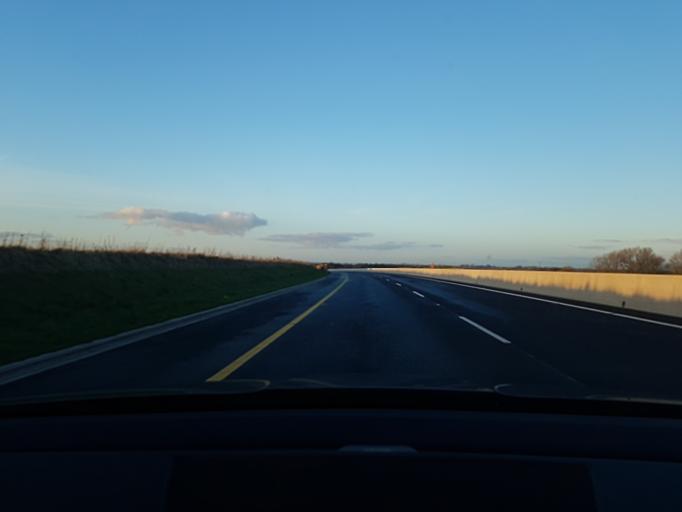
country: IE
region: Connaught
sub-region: County Galway
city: Tuam
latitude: 53.4556
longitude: -8.8476
